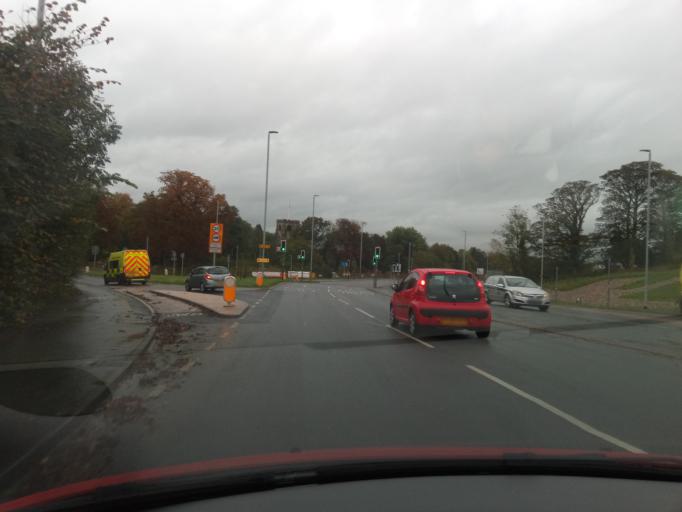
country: GB
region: England
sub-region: Lancashire
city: Preston
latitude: 53.8015
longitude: -2.7172
